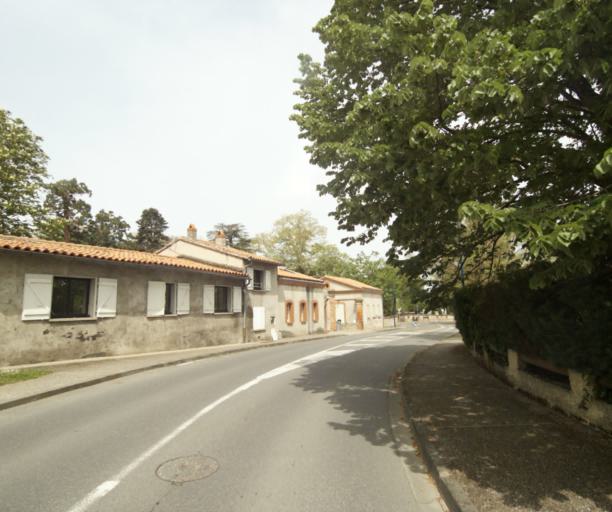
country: FR
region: Midi-Pyrenees
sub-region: Departement de la Haute-Garonne
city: Auzeville-Tolosane
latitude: 43.5248
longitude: 1.4866
